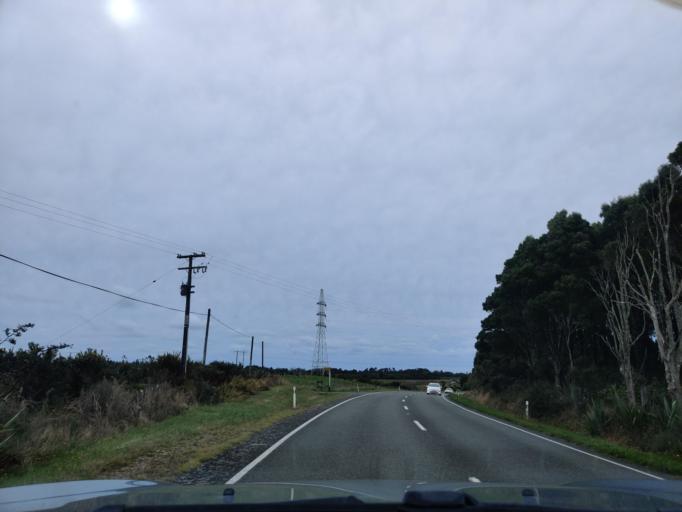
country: NZ
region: West Coast
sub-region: Buller District
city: Westport
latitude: -41.7747
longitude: 171.5927
